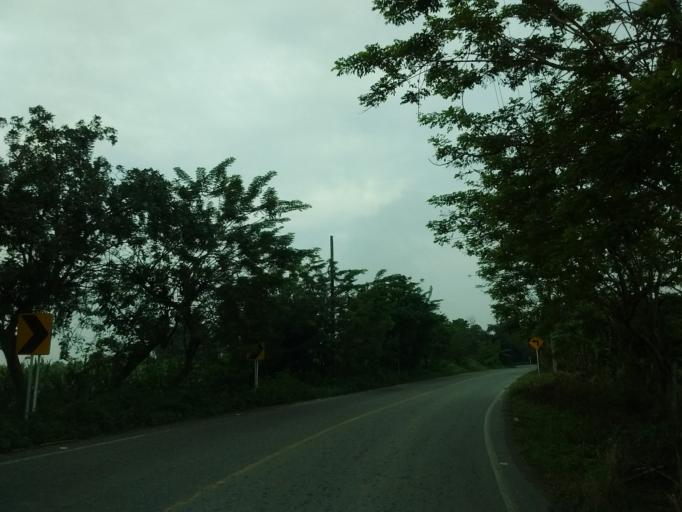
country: CO
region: Cauca
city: Padilla
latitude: 3.2305
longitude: -76.3271
